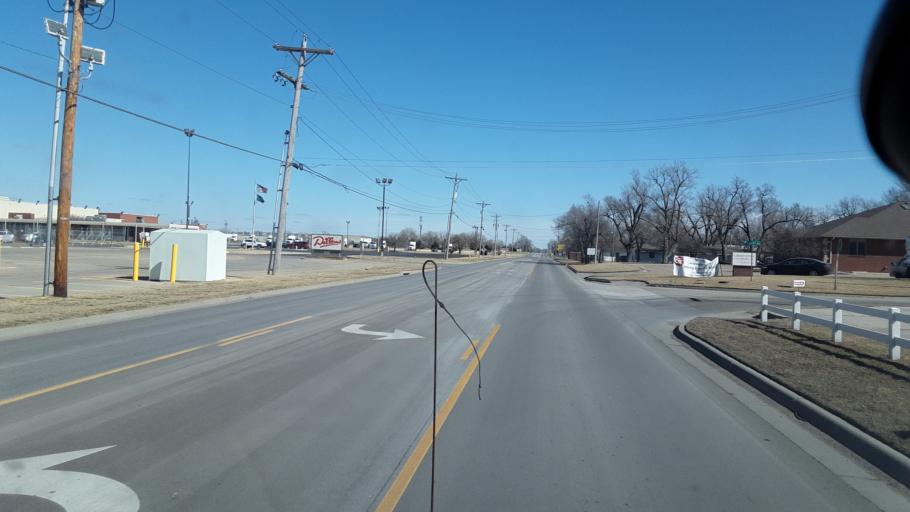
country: US
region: Kansas
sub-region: Reno County
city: Hutchinson
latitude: 38.0577
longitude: -97.8815
